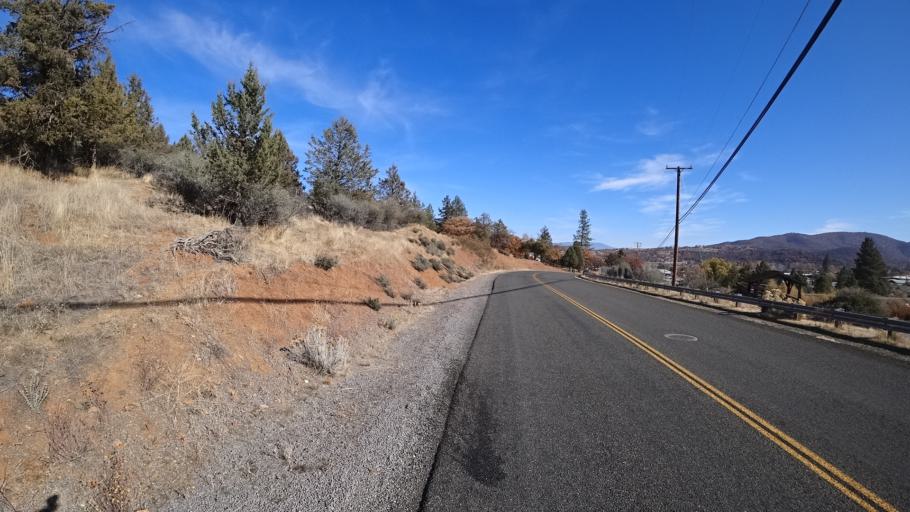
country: US
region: California
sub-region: Siskiyou County
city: Yreka
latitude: 41.7127
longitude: -122.6514
